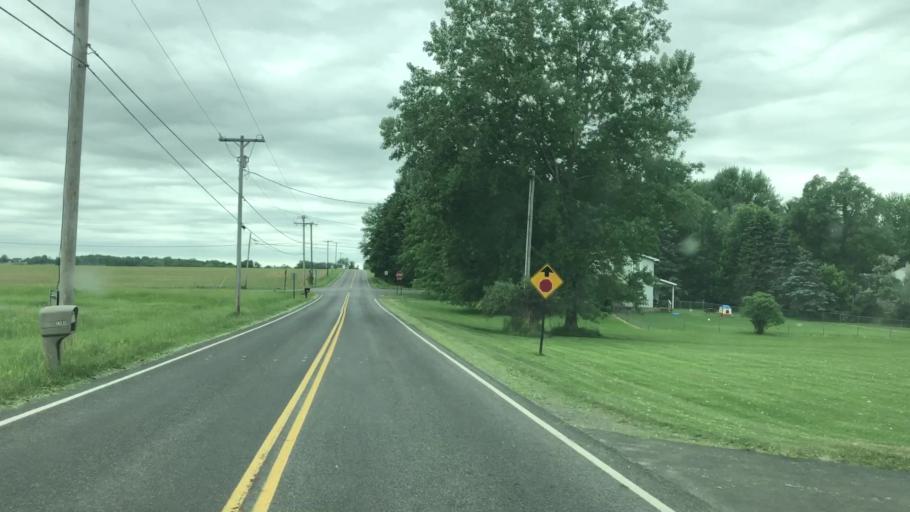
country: US
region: New York
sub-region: Wayne County
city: Macedon
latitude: 43.1163
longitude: -77.3025
